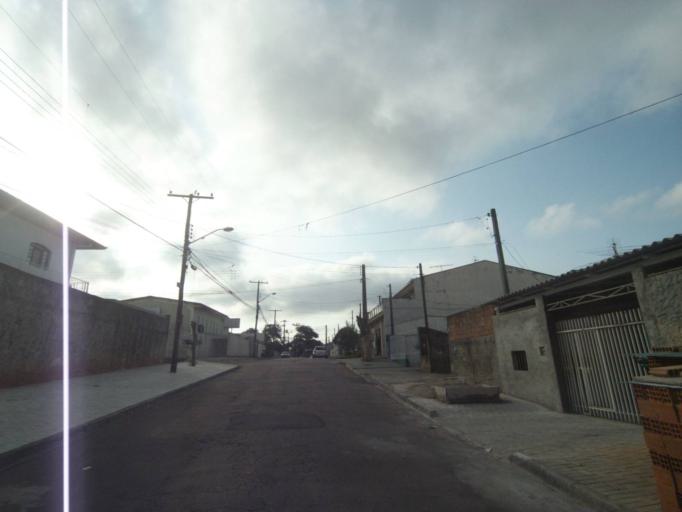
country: BR
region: Parana
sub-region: Sao Jose Dos Pinhais
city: Sao Jose dos Pinhais
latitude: -25.5457
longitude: -49.2598
